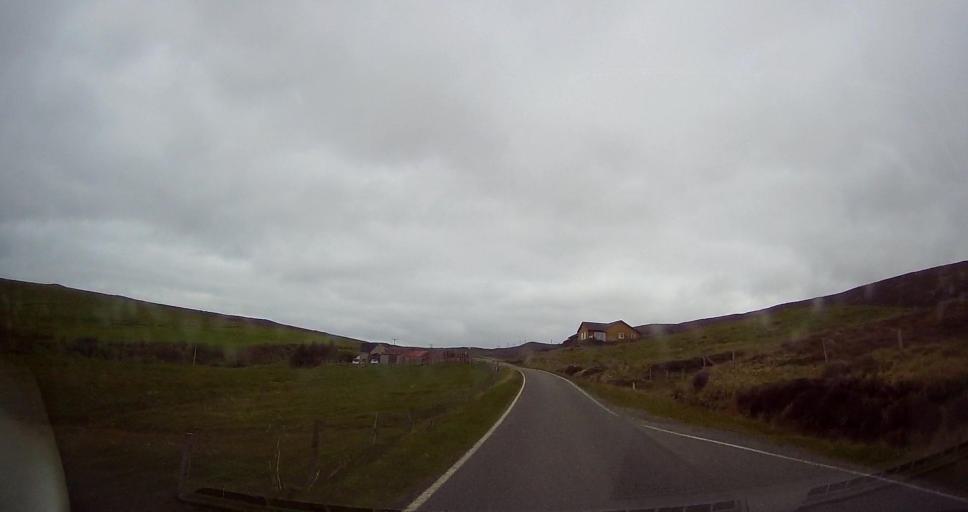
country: GB
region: Scotland
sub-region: Shetland Islands
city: Lerwick
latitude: 60.3044
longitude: -1.3376
